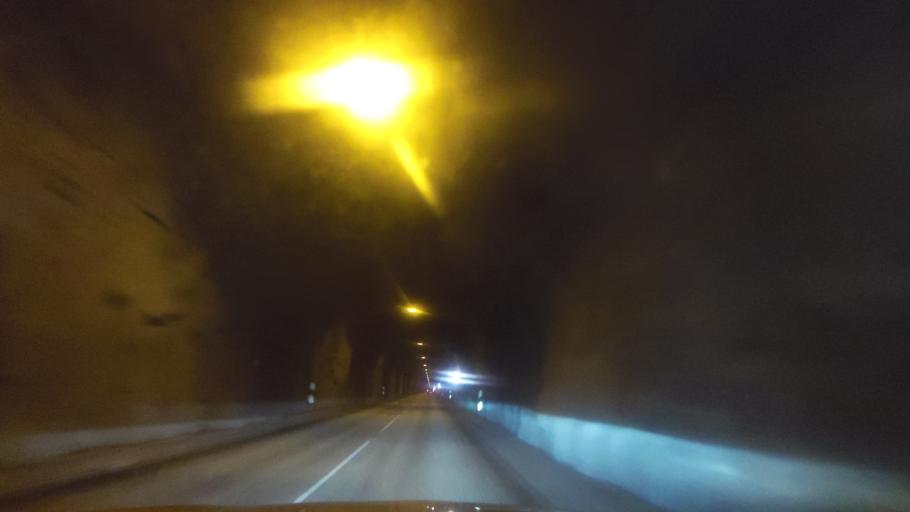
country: IS
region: Westfjords
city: Isafjoerdur
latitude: 66.0572
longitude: -23.2360
